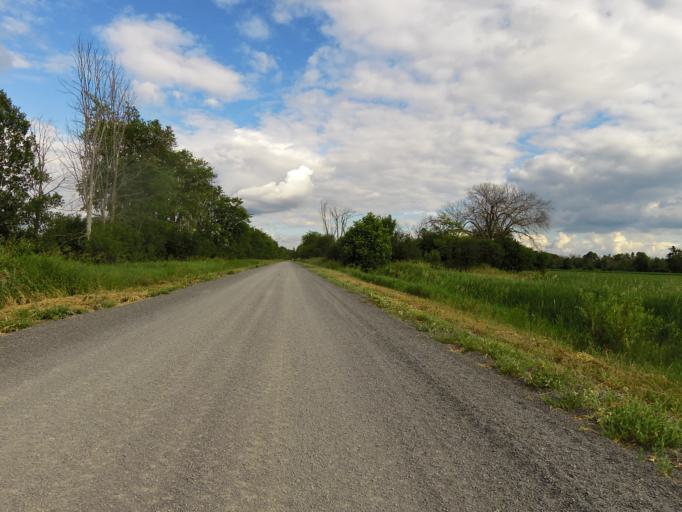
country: CA
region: Ontario
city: Arnprior
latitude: 45.3067
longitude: -76.2737
